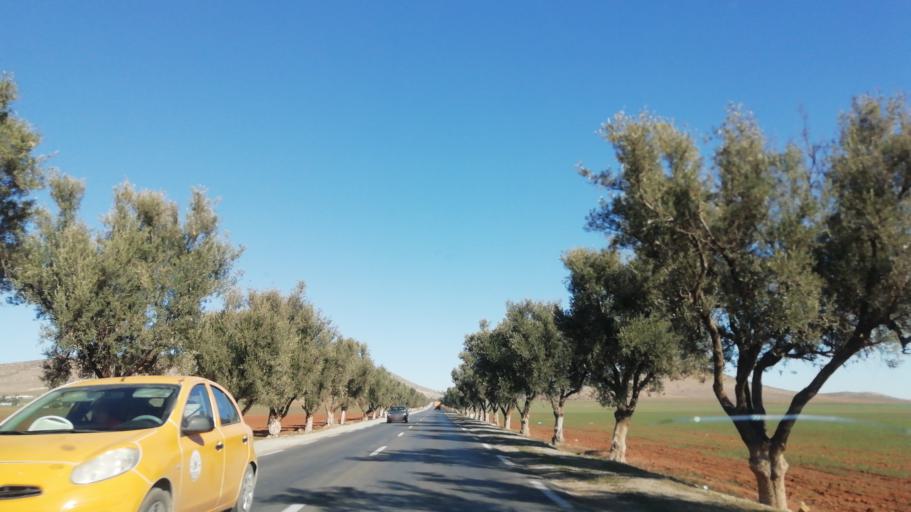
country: DZ
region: Mascara
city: Mascara
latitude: 35.2259
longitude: 0.1143
